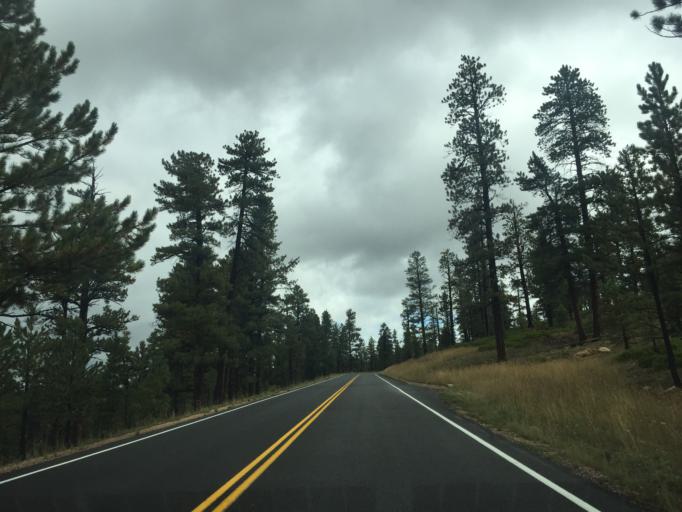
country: US
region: Utah
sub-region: Garfield County
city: Panguitch
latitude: 37.6038
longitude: -112.2066
